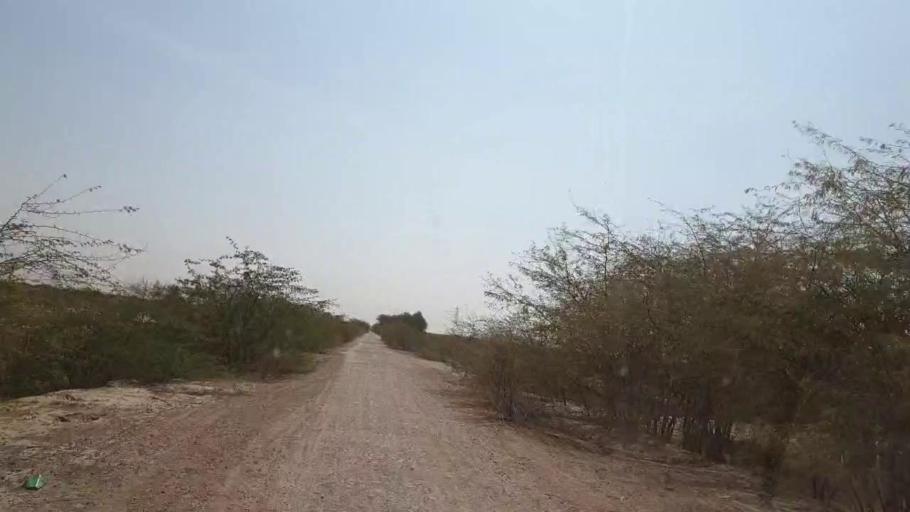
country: PK
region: Sindh
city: Nabisar
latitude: 25.0616
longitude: 69.5526
